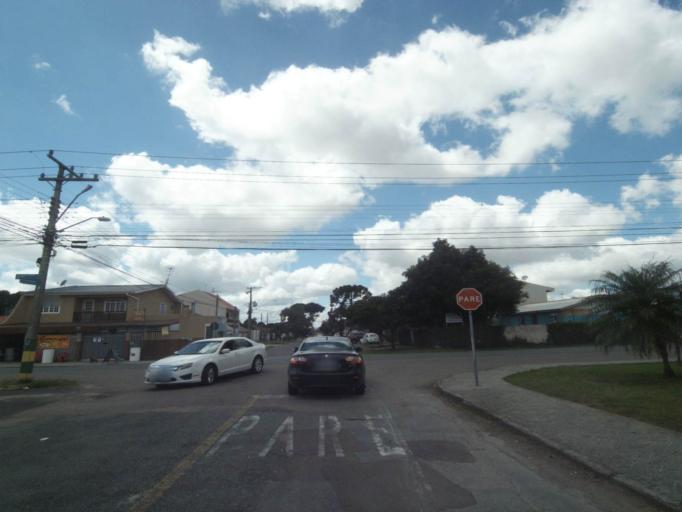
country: BR
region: Parana
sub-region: Pinhais
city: Pinhais
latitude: -25.4378
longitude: -49.2156
